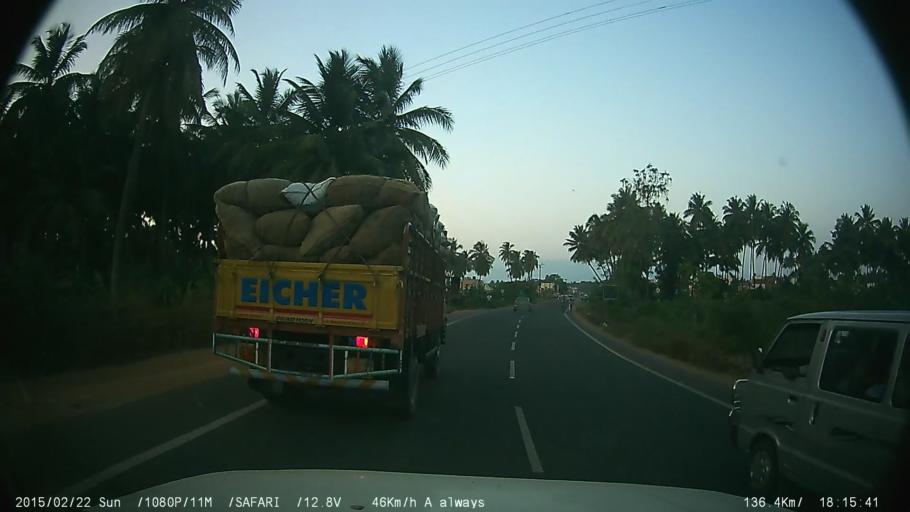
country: IN
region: Tamil Nadu
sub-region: Theni
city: Chinnamanur
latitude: 9.8693
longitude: 77.3925
